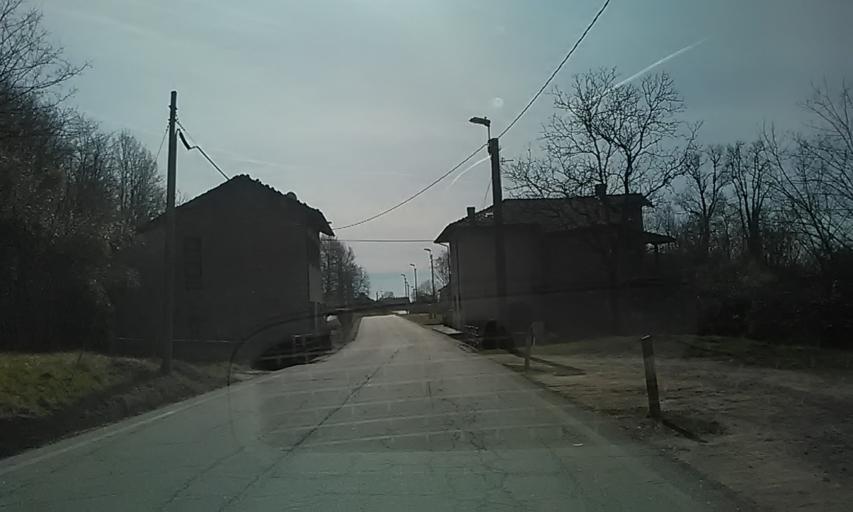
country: IT
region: Piedmont
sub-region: Provincia di Biella
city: Brusnengo
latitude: 45.6018
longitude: 8.2440
